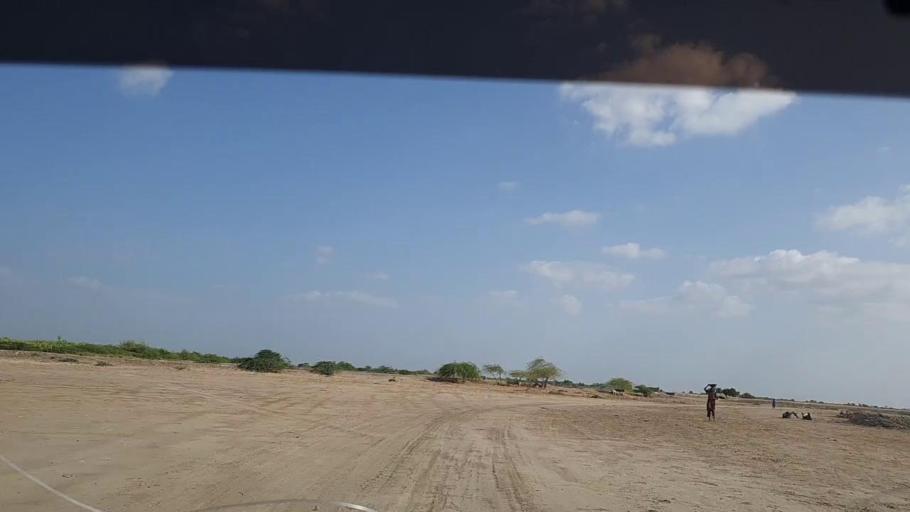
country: PK
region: Sindh
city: Kadhan
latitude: 24.4578
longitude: 68.8577
